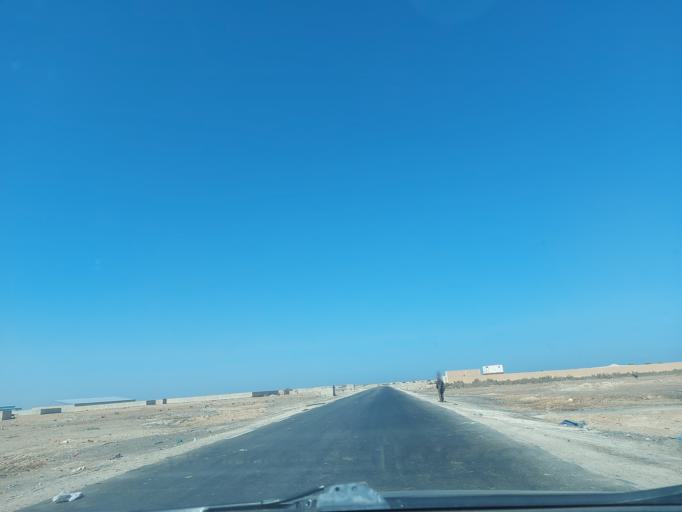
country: MR
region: Nouakchott
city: Nouakchott
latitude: 18.0576
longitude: -16.0153
